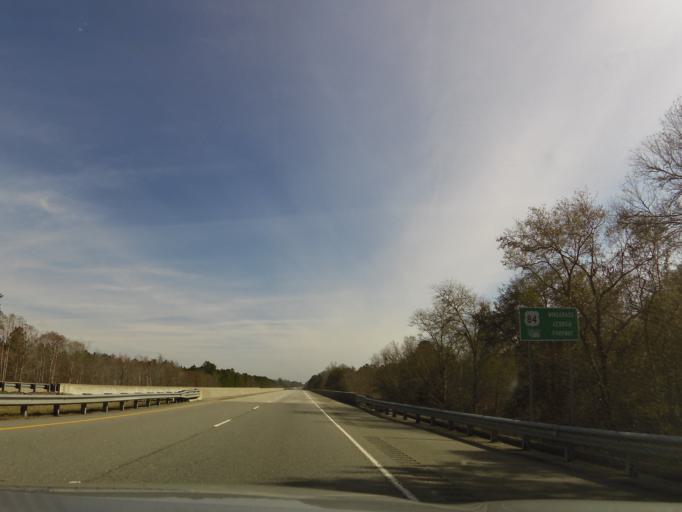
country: US
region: Georgia
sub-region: Lanier County
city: Lakeland
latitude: 30.9254
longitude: -83.0344
